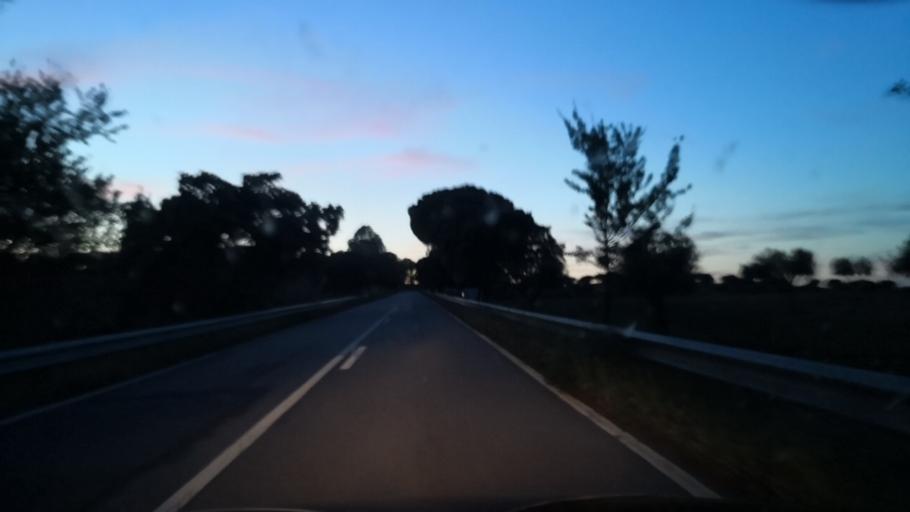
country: ES
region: Extremadura
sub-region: Provincia de Caceres
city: Piedras Albas
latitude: 39.8412
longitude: -6.9754
